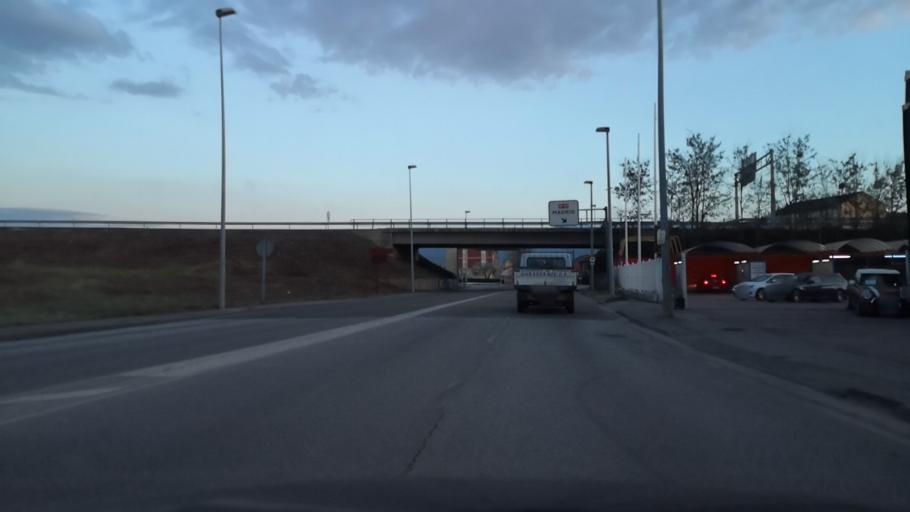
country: ES
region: Castille and Leon
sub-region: Provincia de Leon
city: Ponferrada
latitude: 42.5693
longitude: -6.6072
